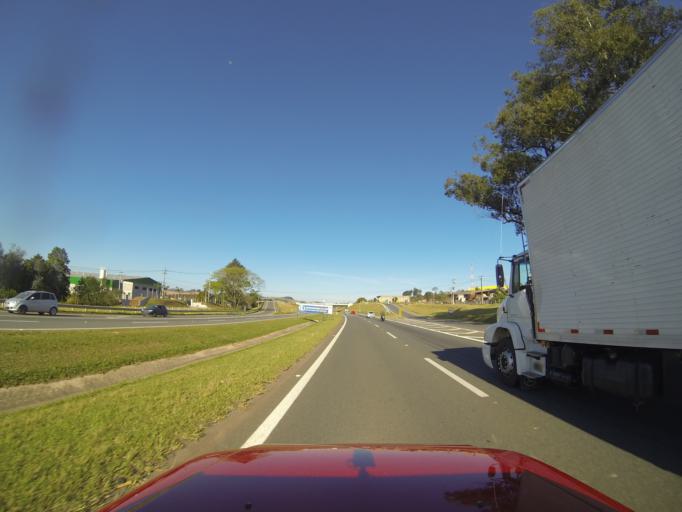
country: BR
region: Sao Paulo
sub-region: Bom Jesus Dos Perdoes
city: Bom Jesus dos Perdoes
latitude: -23.1150
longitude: -46.4867
